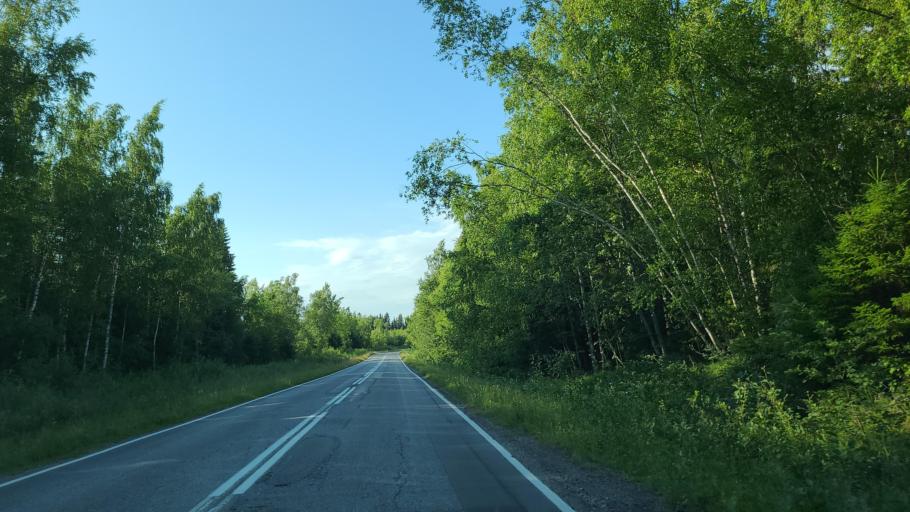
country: FI
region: Ostrobothnia
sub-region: Vaasa
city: Replot
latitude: 63.3014
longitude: 21.3590
